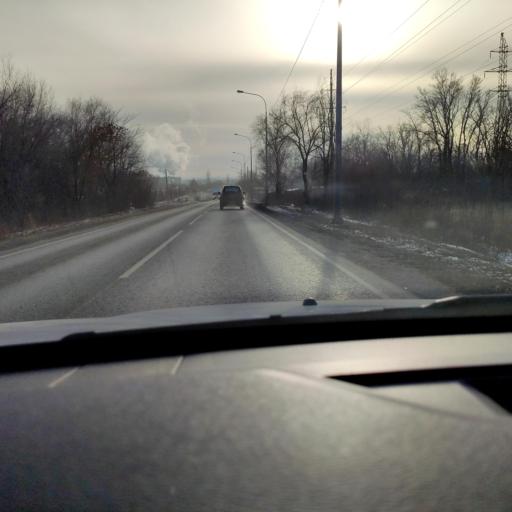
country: RU
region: Samara
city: Petra-Dubrava
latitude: 53.2729
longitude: 50.3837
